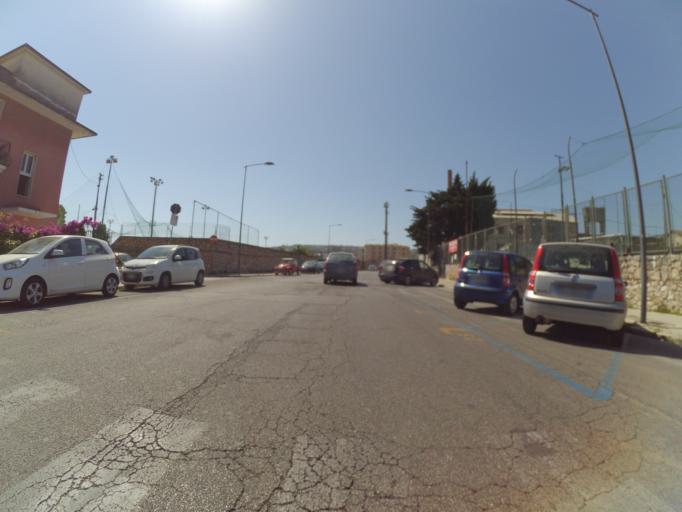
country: IT
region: Latium
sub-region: Provincia di Latina
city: Gaeta
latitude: 41.2114
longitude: 13.5682
